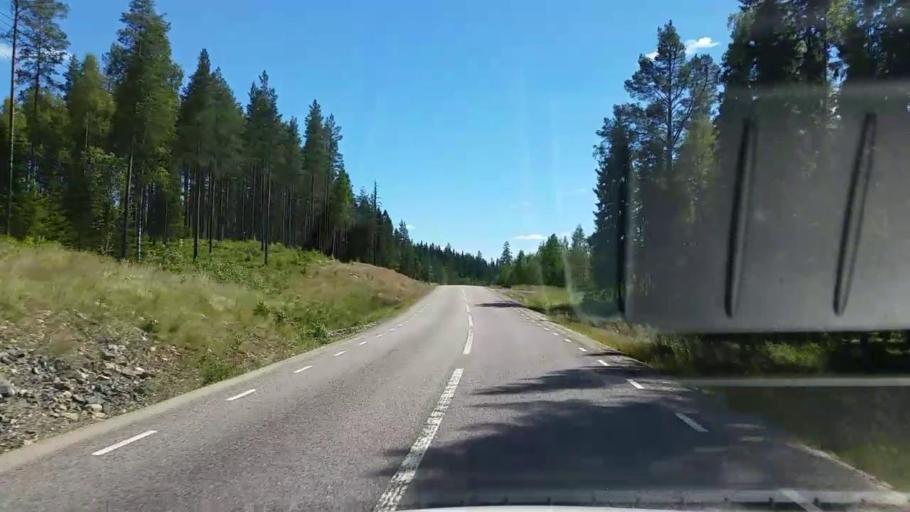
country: SE
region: Gaevleborg
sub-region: Ovanakers Kommun
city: Edsbyn
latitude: 61.5132
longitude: 15.6793
